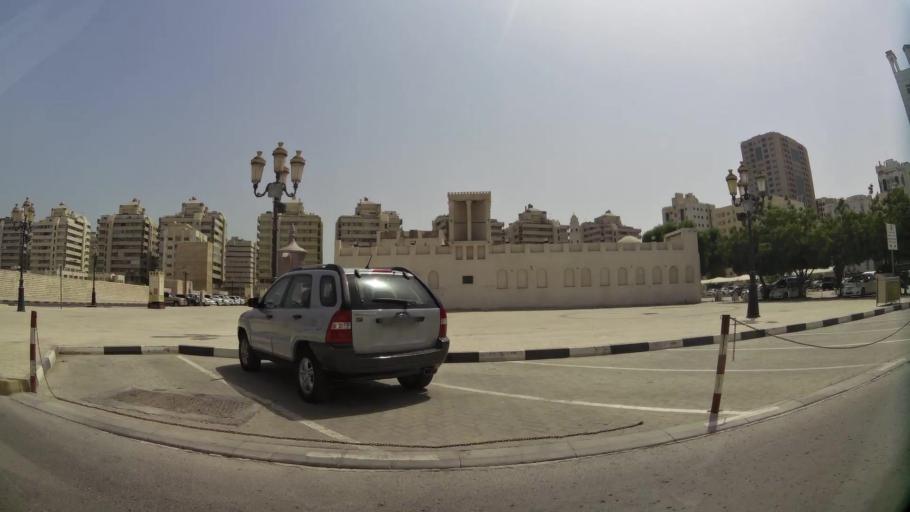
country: AE
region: Ash Shariqah
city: Sharjah
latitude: 25.3566
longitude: 55.3852
